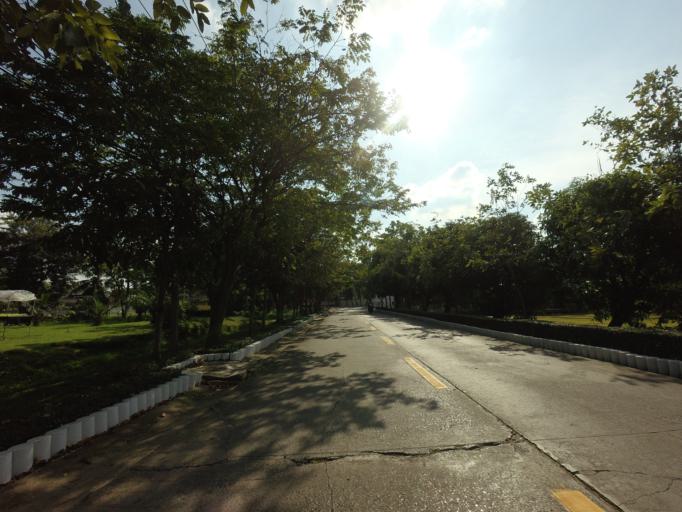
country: TH
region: Bangkok
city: Din Daeng
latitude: 13.7765
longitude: 100.5500
